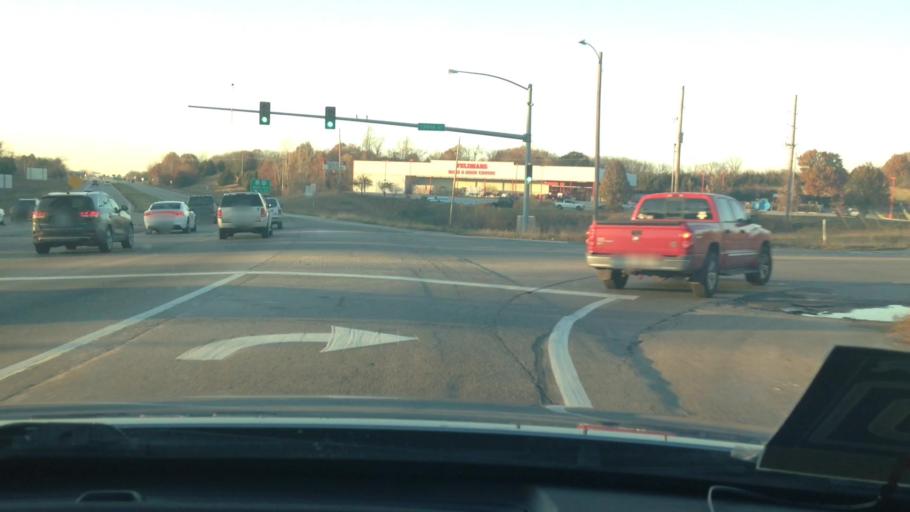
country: US
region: Kansas
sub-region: Wyandotte County
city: Bonner Springs
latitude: 39.1042
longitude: -94.8808
